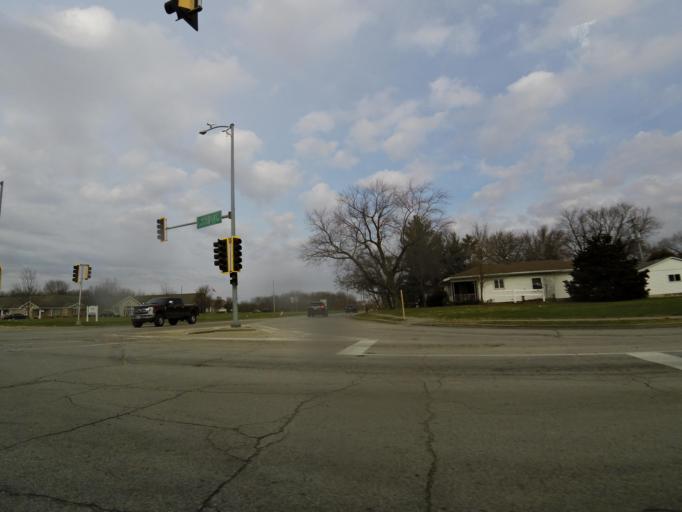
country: US
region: Illinois
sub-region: Christian County
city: Pana
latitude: 39.3902
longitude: -89.0721
